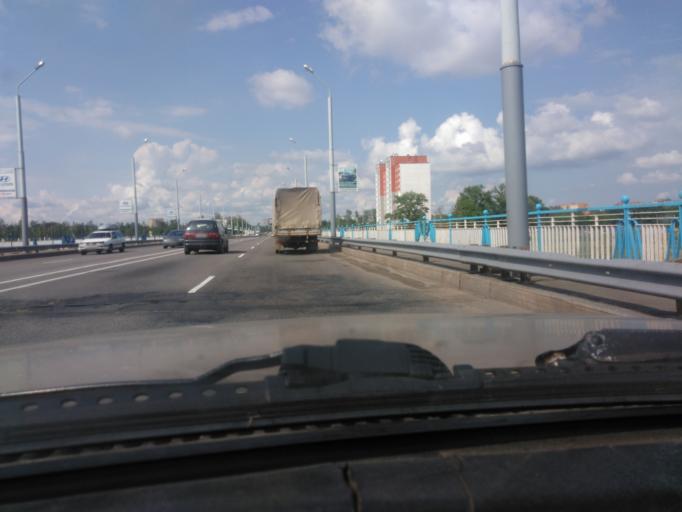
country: BY
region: Mogilev
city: Mahilyow
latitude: 53.9207
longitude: 30.3494
